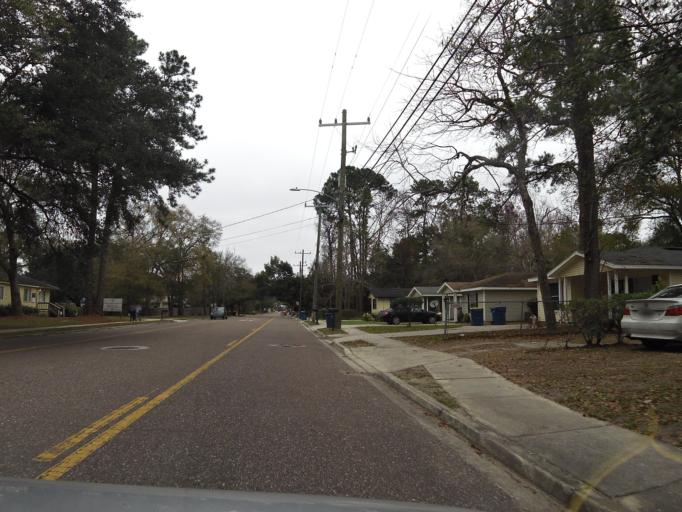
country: US
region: Florida
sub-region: Duval County
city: Jacksonville
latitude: 30.3671
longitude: -81.6989
